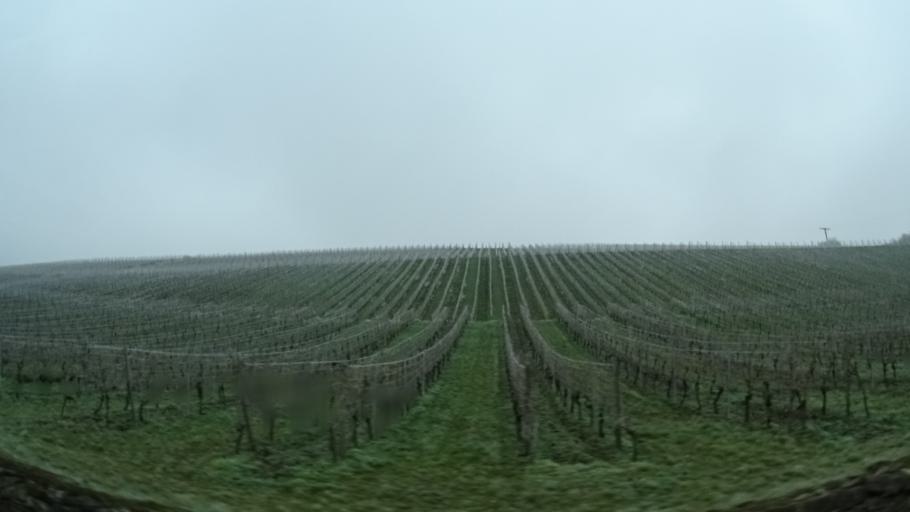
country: DE
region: Bavaria
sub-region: Regierungsbezirk Unterfranken
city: Frickenhausen
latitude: 49.6704
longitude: 10.1067
